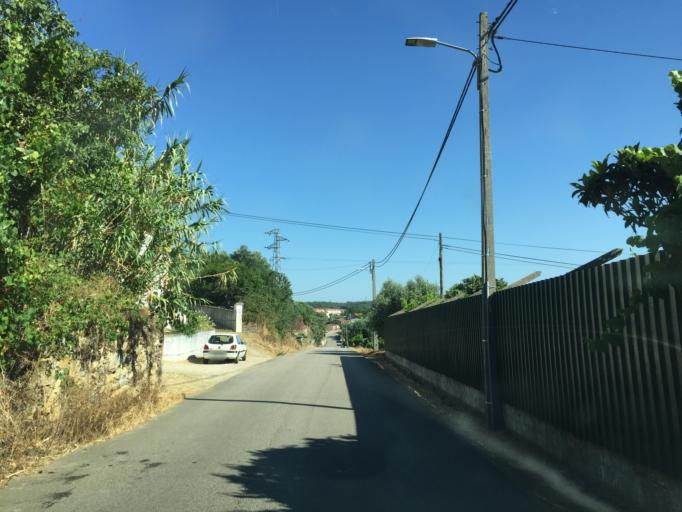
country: PT
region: Santarem
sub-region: Tomar
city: Tomar
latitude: 39.5977
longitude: -8.3255
